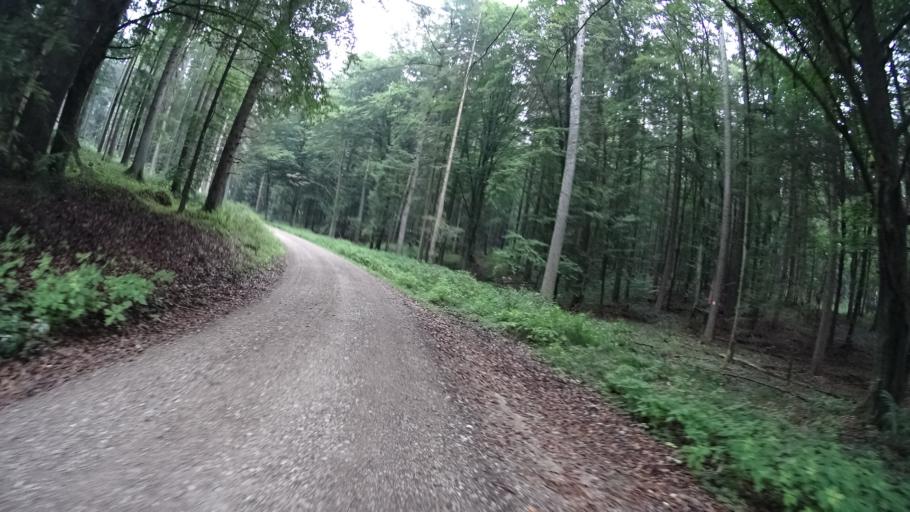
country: DE
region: Bavaria
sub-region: Upper Bavaria
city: Stammham
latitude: 48.8682
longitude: 11.4987
